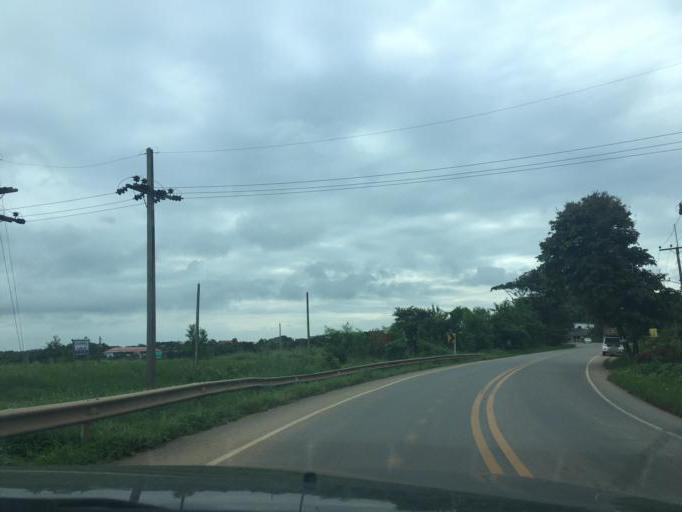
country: TH
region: Chiang Rai
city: Chiang Rai
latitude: 20.0052
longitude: 99.8799
